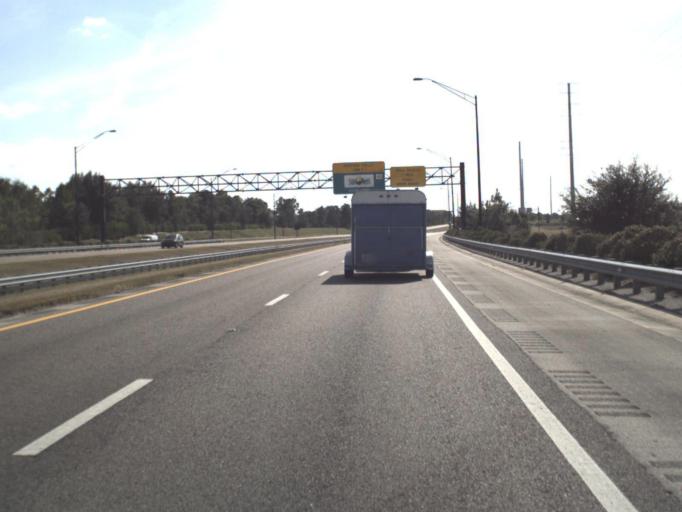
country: US
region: Florida
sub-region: Polk County
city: Citrus Ridge
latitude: 28.3759
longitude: -81.6110
